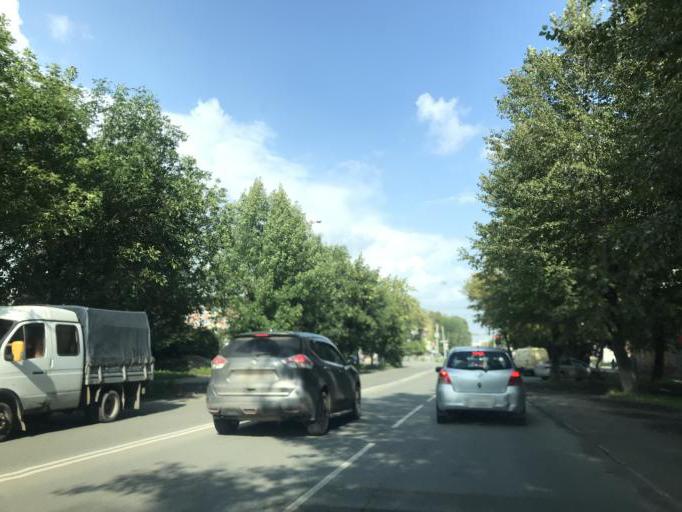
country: RU
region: Chelyabinsk
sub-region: Gorod Chelyabinsk
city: Chelyabinsk
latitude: 55.1808
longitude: 61.4446
